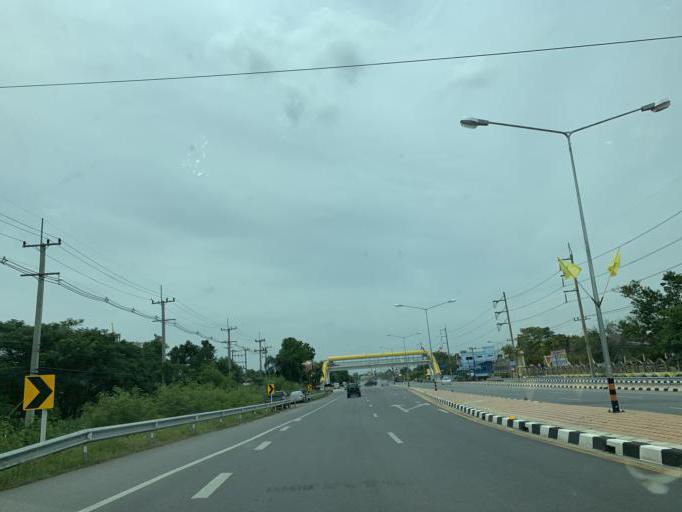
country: TH
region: Uthai Thani
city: Uthai Thani
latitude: 15.4020
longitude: 100.0299
